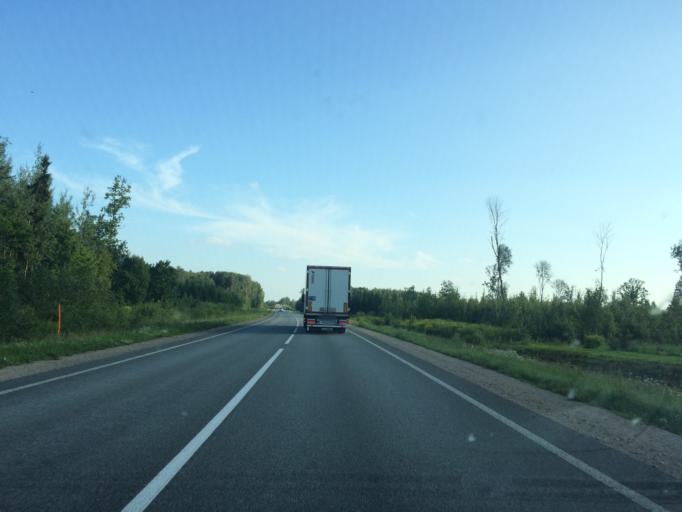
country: LV
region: Koknese
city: Koknese
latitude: 56.6578
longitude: 25.4596
